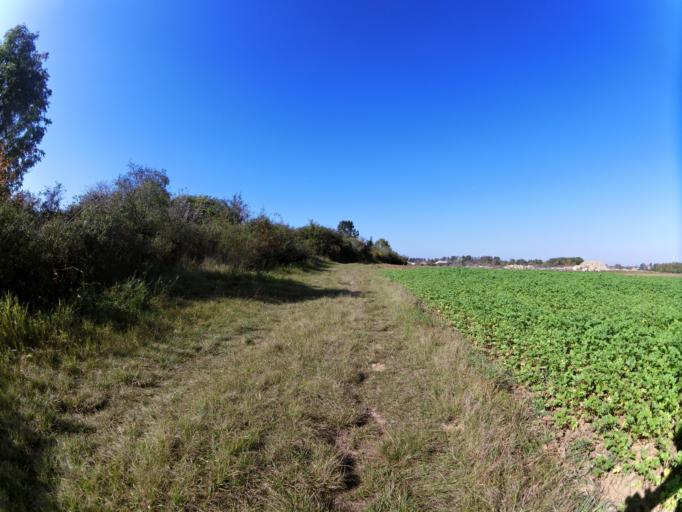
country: DE
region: Bavaria
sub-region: Regierungsbezirk Unterfranken
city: Sommerhausen
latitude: 49.6853
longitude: 10.0407
